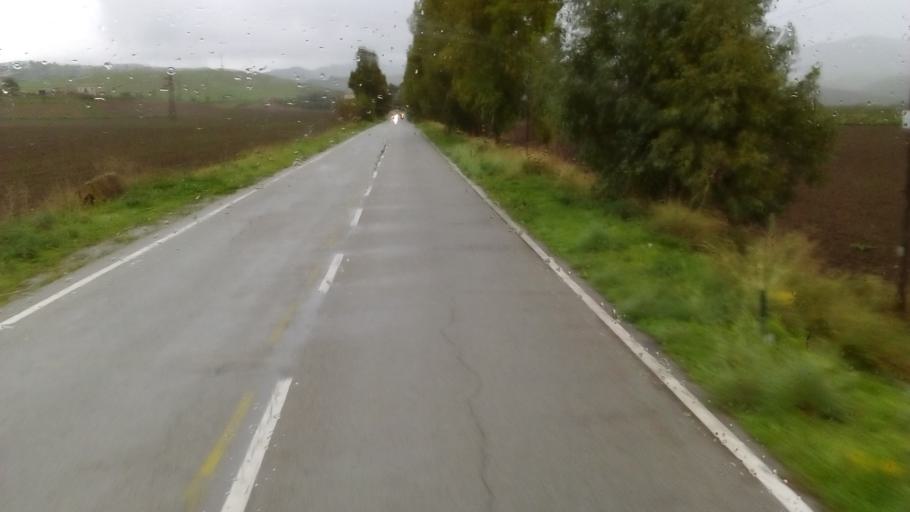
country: IT
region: Sicily
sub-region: Enna
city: Pietraperzia
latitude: 37.4888
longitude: 14.1549
